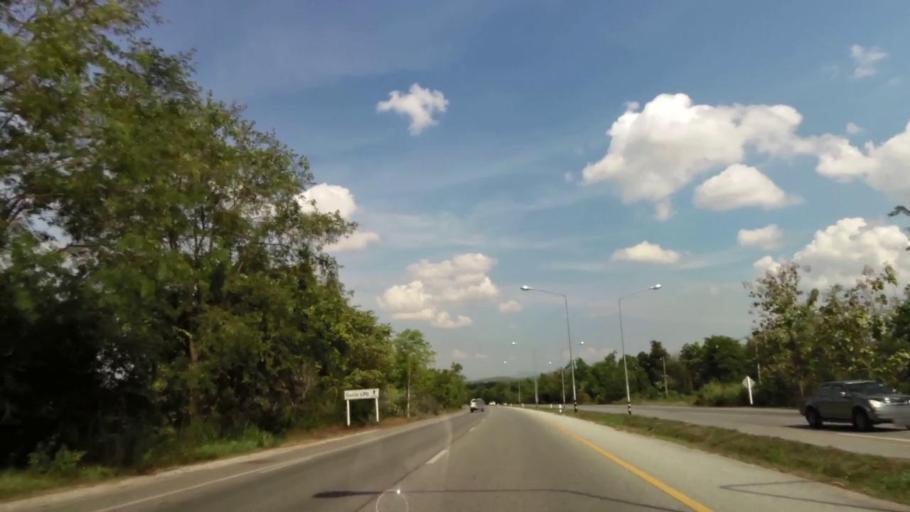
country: TH
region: Uttaradit
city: Thong Saen Khan
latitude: 17.4536
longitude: 100.2372
